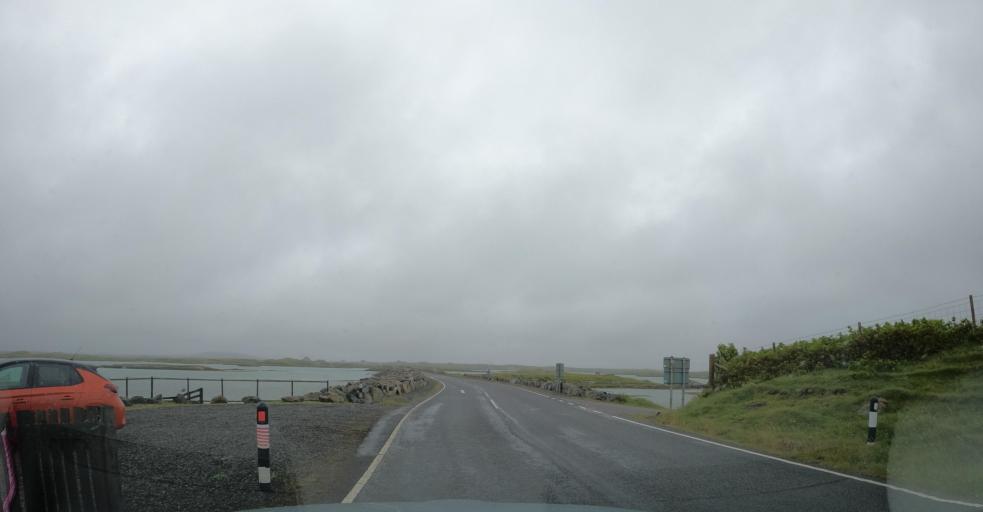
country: GB
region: Scotland
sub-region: Eilean Siar
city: Benbecula
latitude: 57.5002
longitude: -7.2638
